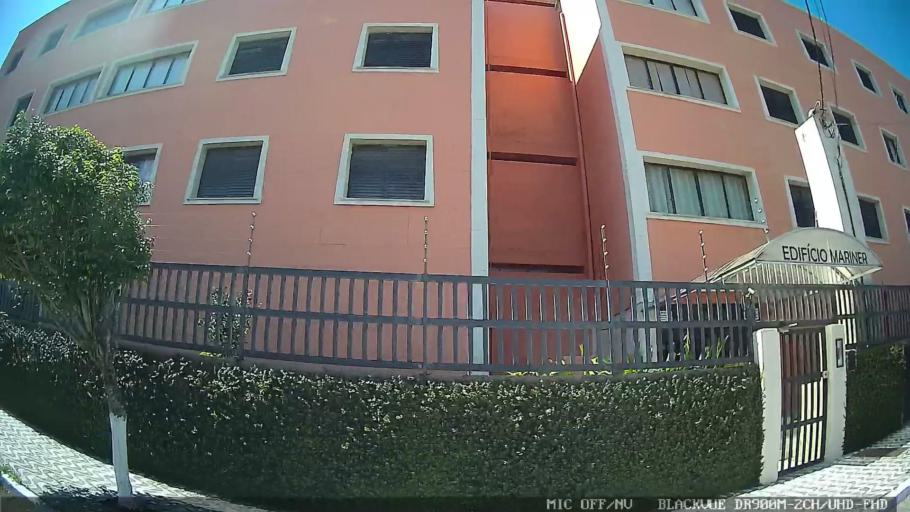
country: BR
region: Sao Paulo
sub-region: Peruibe
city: Peruibe
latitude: -24.2989
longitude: -46.9726
